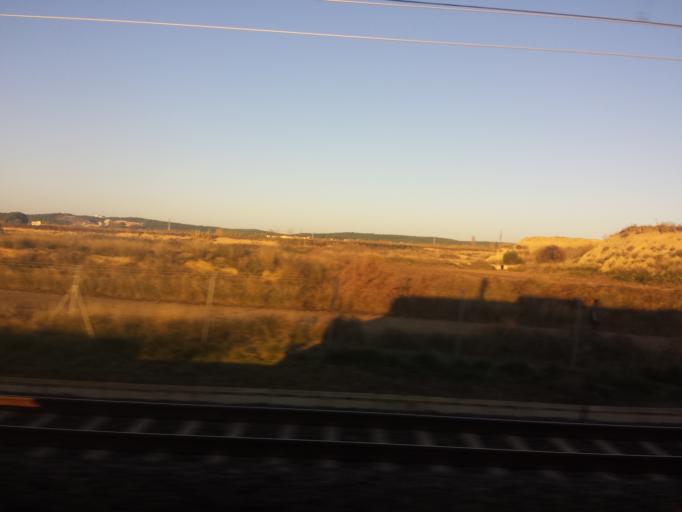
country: ES
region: Aragon
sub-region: Provincia de Zaragoza
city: Zaragoza
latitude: 41.7094
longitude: -0.8492
